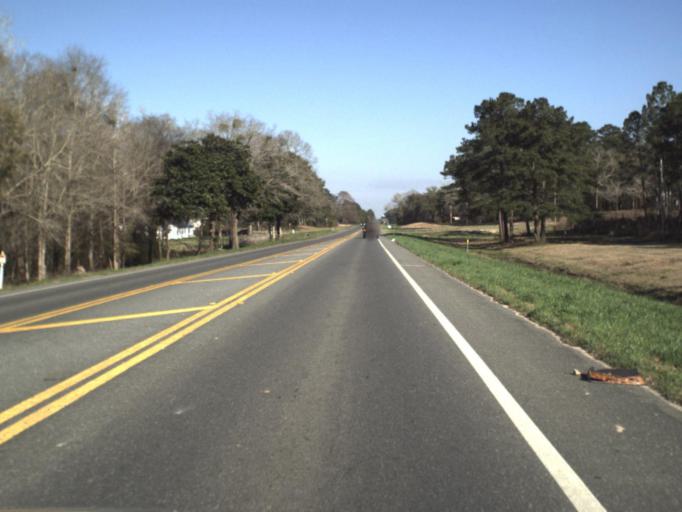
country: US
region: Florida
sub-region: Jackson County
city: Marianna
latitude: 30.7845
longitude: -85.2909
